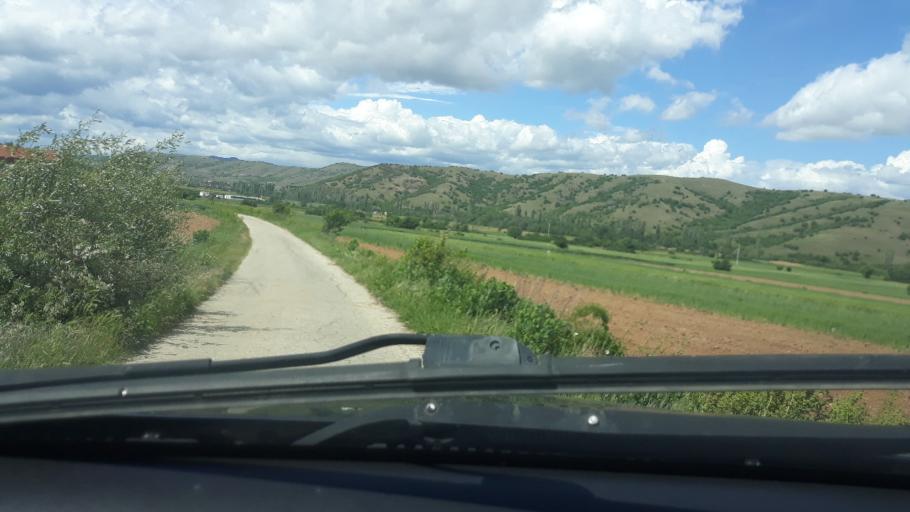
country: MK
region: Krivogastani
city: Krivogashtani
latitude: 41.3385
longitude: 21.3007
